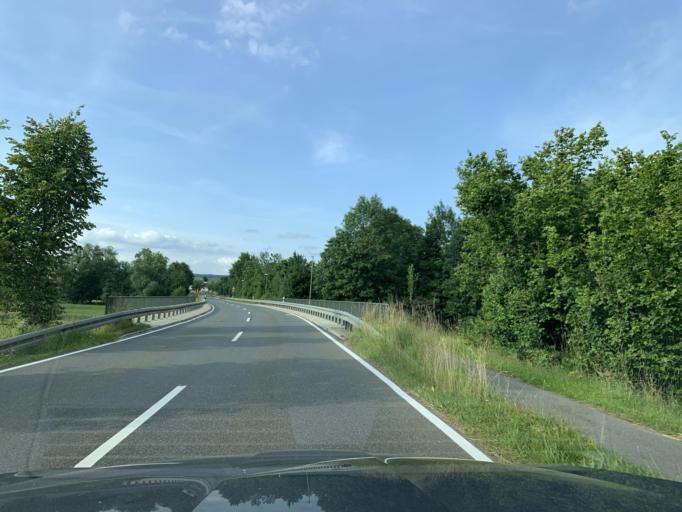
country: DE
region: Bavaria
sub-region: Upper Palatinate
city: Schwarzhofen
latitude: 49.3763
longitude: 12.3397
